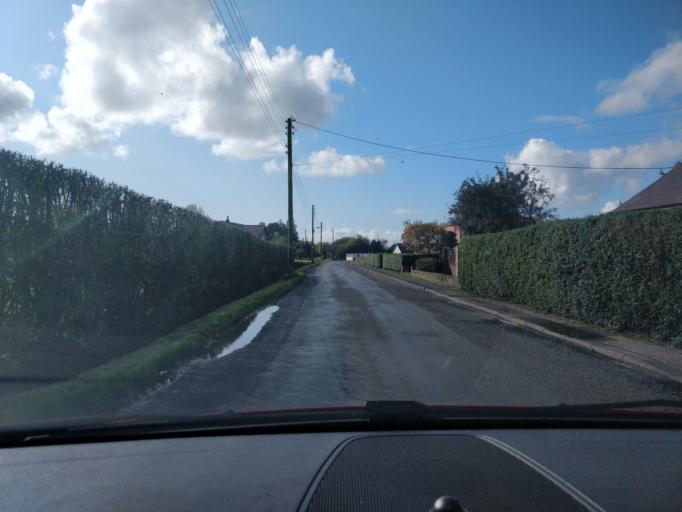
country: GB
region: England
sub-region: Lancashire
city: Tarleton
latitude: 53.6787
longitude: -2.8463
